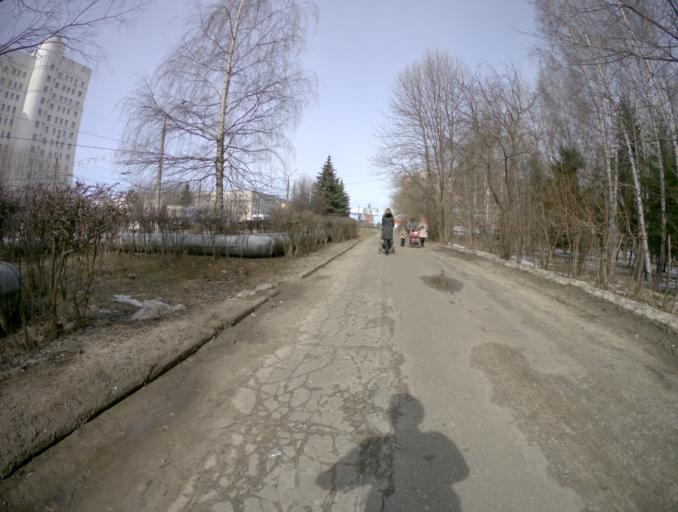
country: RU
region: Vladimir
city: Kommunar
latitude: 56.1673
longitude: 40.4655
